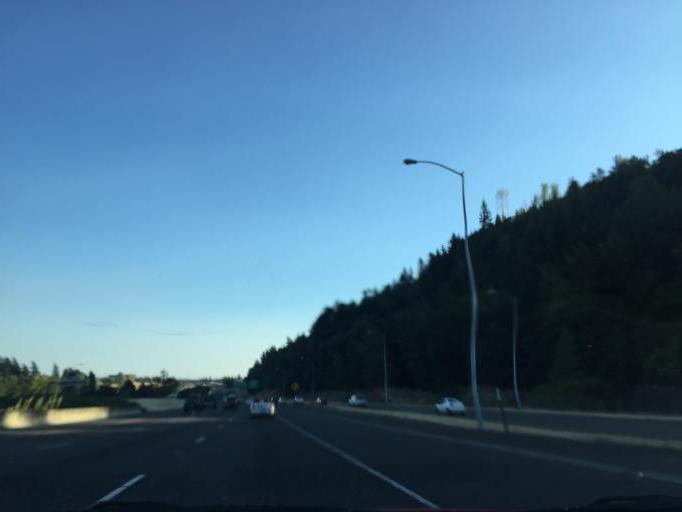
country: US
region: Oregon
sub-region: Multnomah County
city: Lents
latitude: 45.5435
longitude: -122.5618
